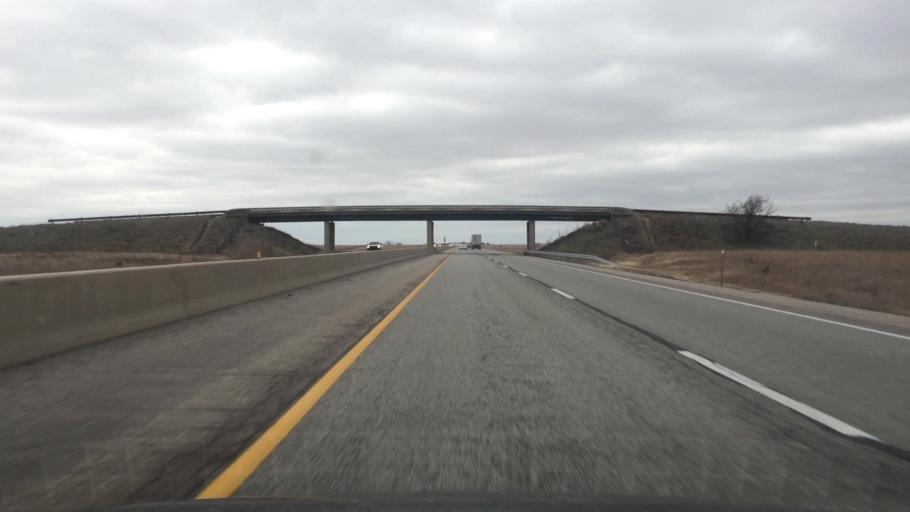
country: US
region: Kansas
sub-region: Butler County
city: El Dorado
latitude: 38.0146
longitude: -96.6751
